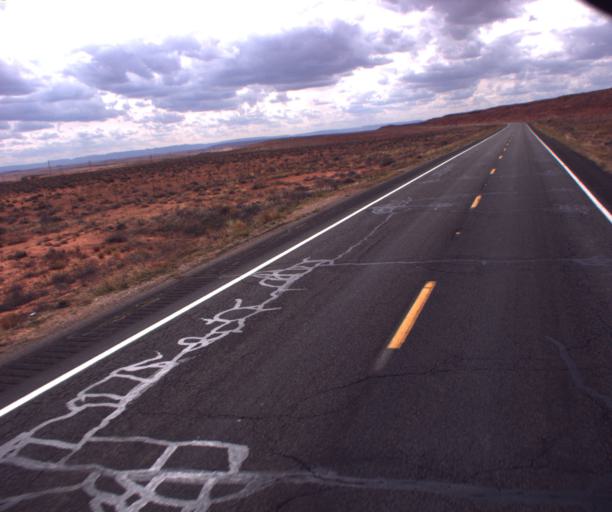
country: US
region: Arizona
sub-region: Navajo County
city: Kayenta
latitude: 36.9142
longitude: -109.7760
